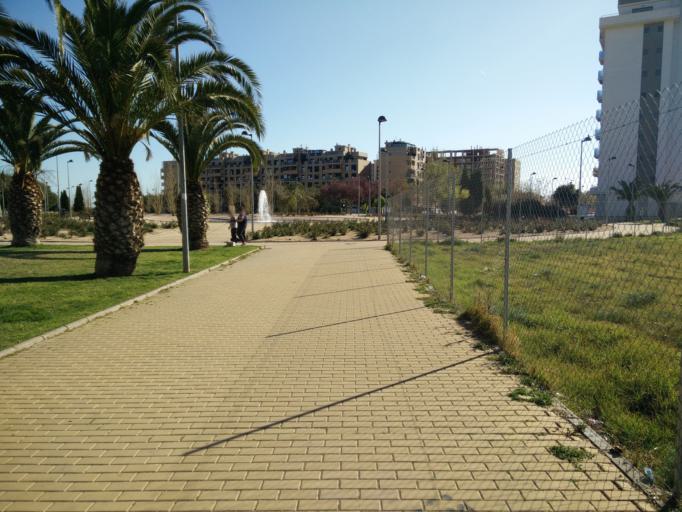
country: ES
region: Valencia
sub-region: Provincia de Castello
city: Castello de la Plana
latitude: 39.9764
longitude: -0.0382
